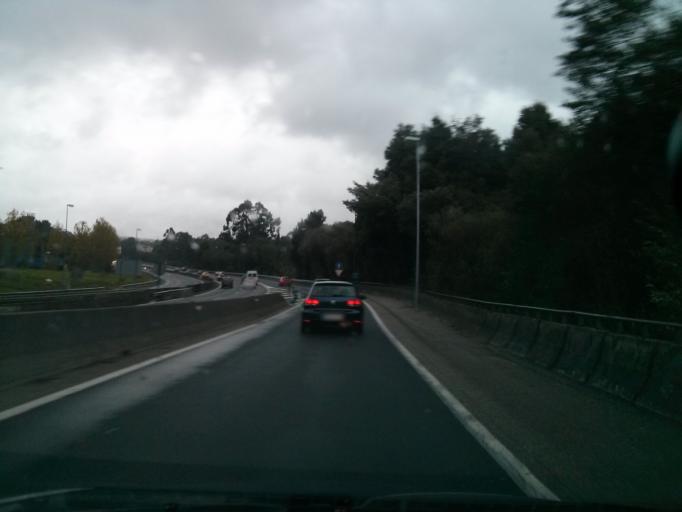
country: ES
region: Galicia
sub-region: Provincia de Pontevedra
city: Porrino
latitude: 42.1718
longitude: -8.6224
